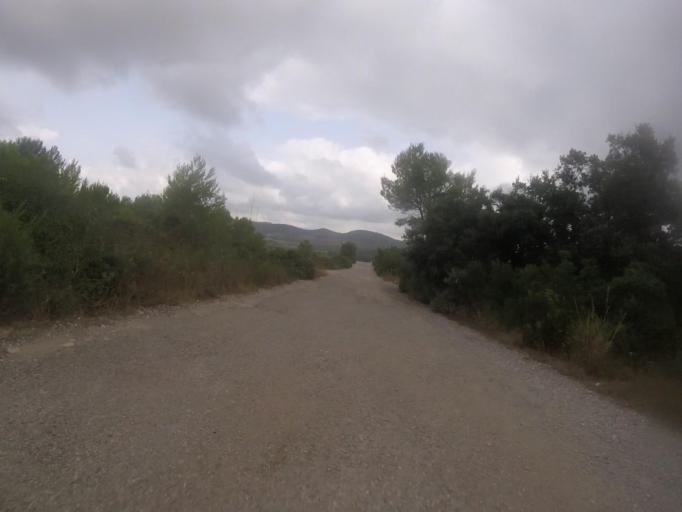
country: ES
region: Valencia
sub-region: Provincia de Castello
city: Santa Magdalena de Pulpis
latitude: 40.3406
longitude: 0.2739
